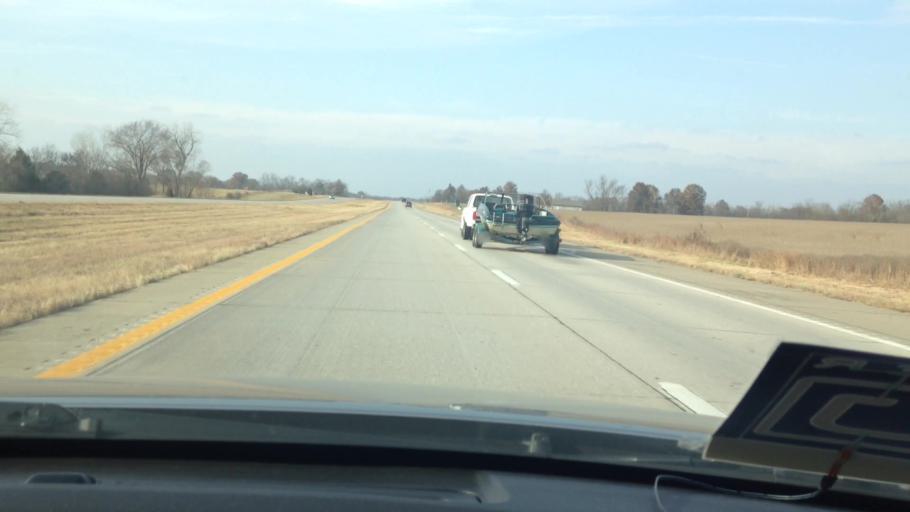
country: US
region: Missouri
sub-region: Henry County
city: Clinton
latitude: 38.4520
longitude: -93.9612
